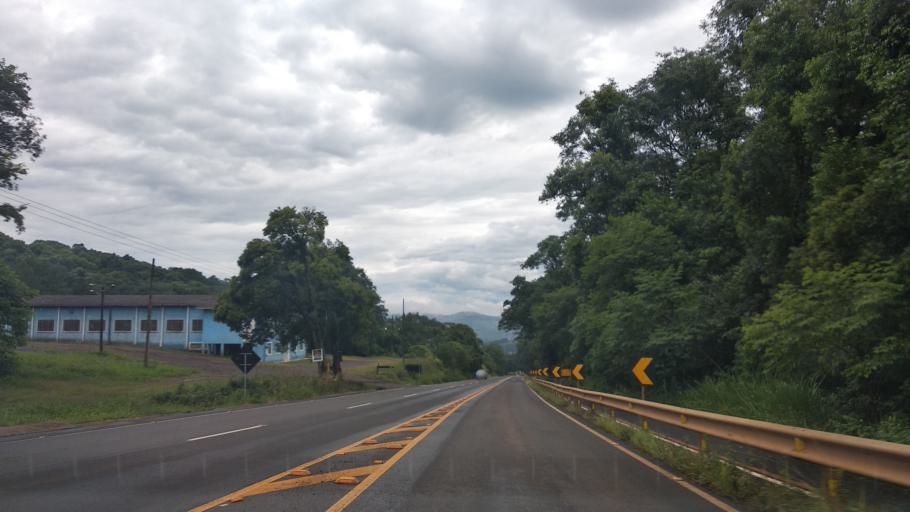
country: BR
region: Santa Catarina
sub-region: Videira
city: Videira
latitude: -27.0800
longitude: -51.2359
